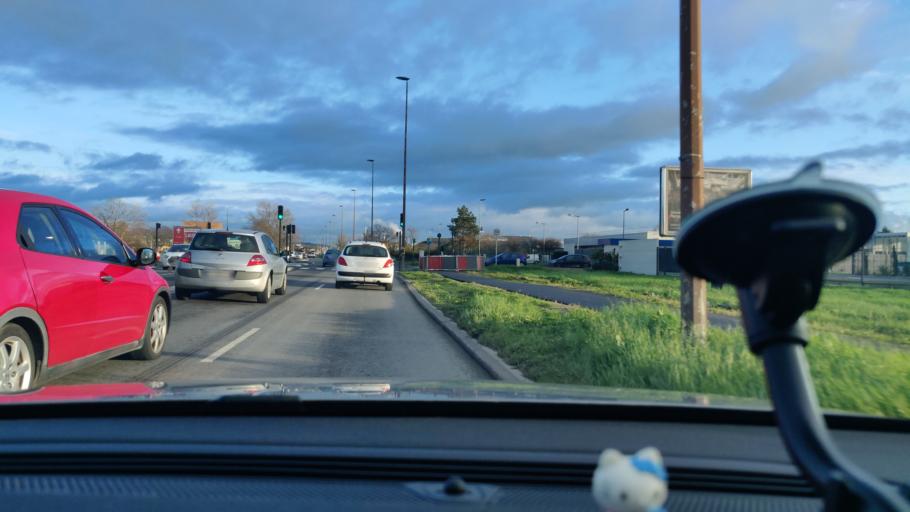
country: FR
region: Midi-Pyrenees
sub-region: Departement de la Haute-Garonne
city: Cugnaux
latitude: 43.5666
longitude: 1.3788
